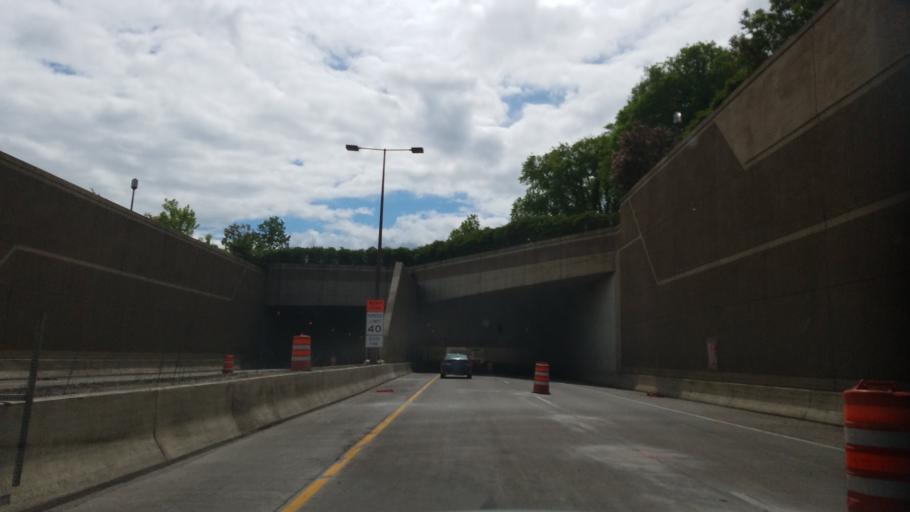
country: US
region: Minnesota
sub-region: Saint Louis County
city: Duluth
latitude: 46.7958
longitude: -92.0861
